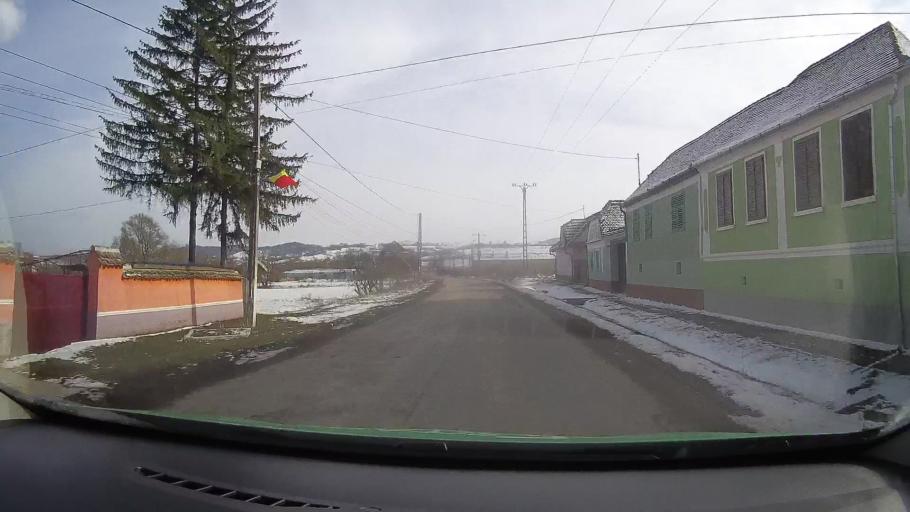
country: RO
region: Mures
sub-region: Comuna Apold
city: Apold
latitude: 46.1223
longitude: 24.8199
